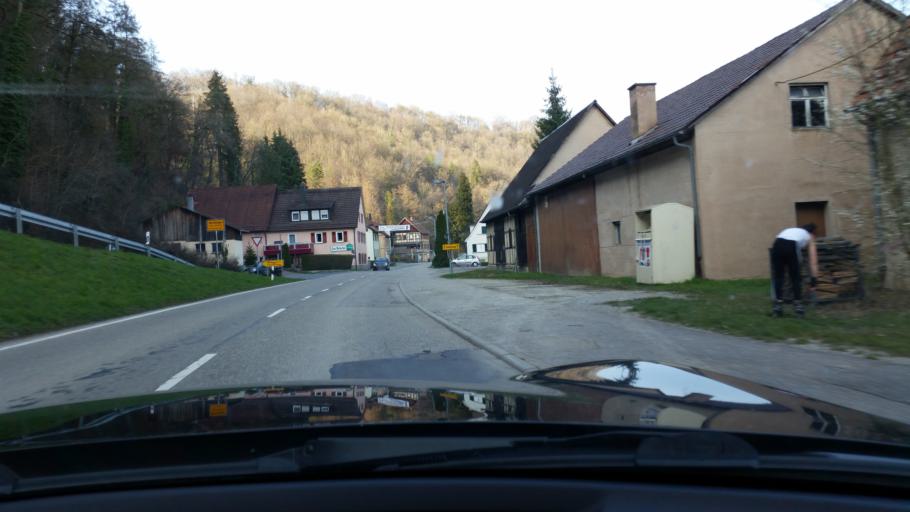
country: DE
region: Baden-Wuerttemberg
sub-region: Regierungsbezirk Stuttgart
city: Jagsthausen
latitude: 49.3281
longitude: 9.4835
